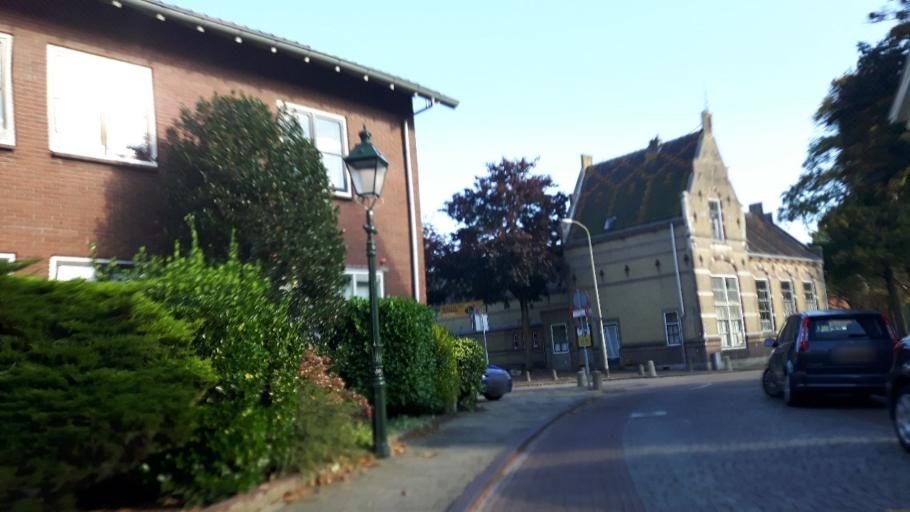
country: NL
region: Utrecht
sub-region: Gemeente Oudewater
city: Oudewater
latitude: 52.0213
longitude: 4.8739
